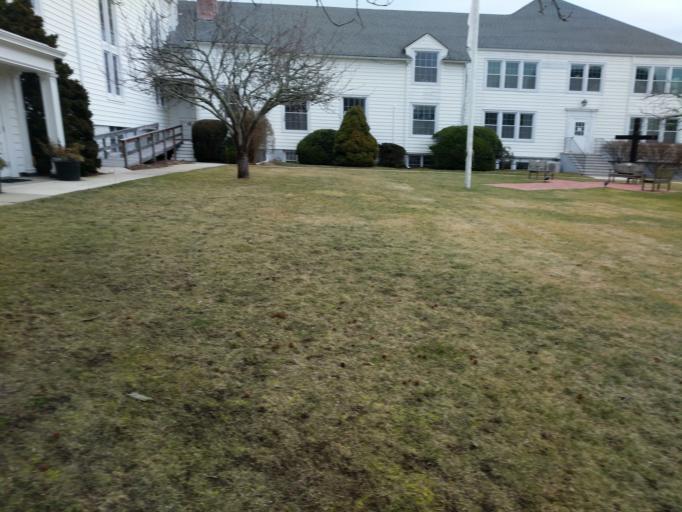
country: US
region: New York
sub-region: Suffolk County
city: Southampton
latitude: 40.8839
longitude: -72.3893
